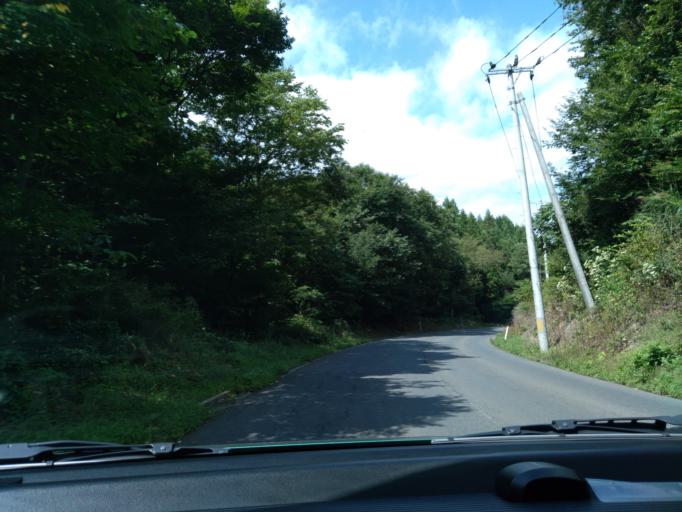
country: JP
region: Iwate
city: Morioka-shi
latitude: 39.5957
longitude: 141.0893
